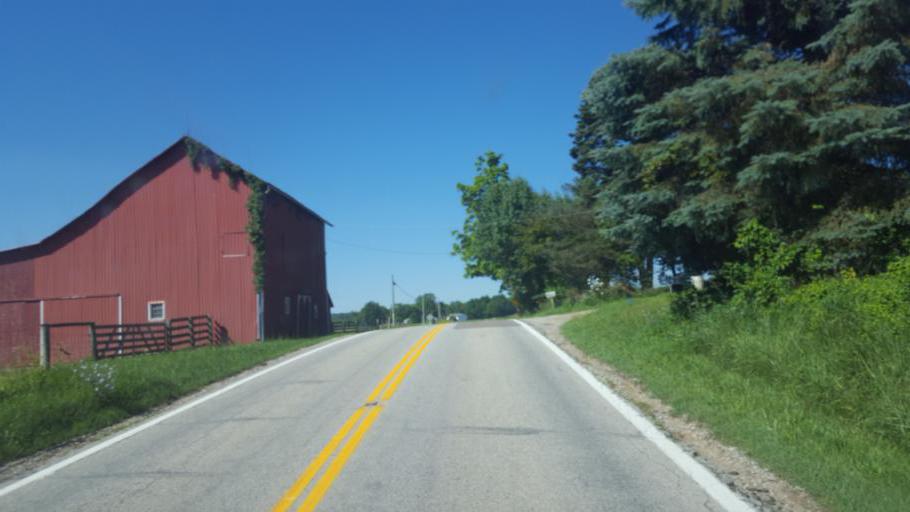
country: US
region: Ohio
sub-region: Knox County
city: Fredericktown
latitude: 40.4711
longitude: -82.6889
